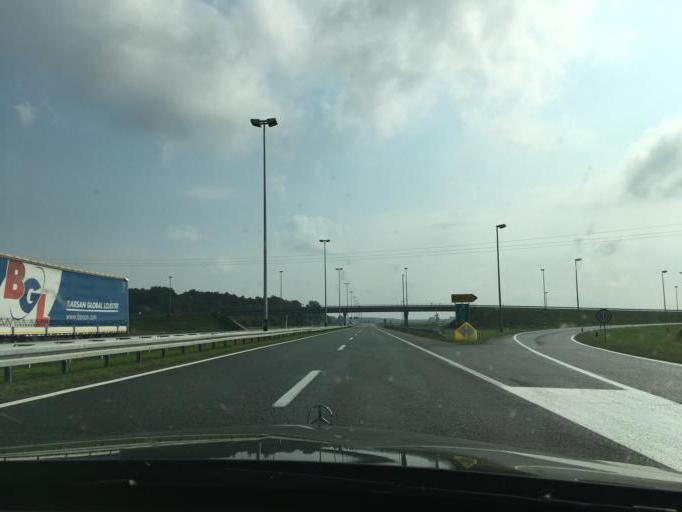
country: HR
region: Brodsko-Posavska
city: Bukovlje
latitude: 45.1786
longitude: 18.0663
